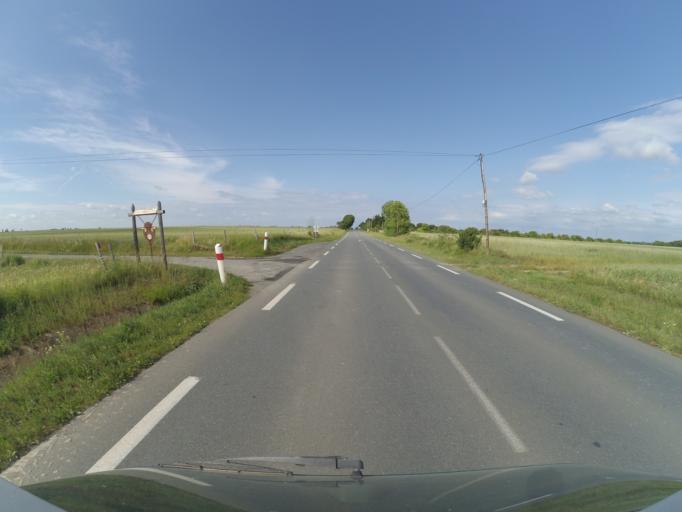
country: FR
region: Poitou-Charentes
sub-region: Departement de la Charente-Maritime
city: Saint-Xandre
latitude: 46.2306
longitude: -1.0780
